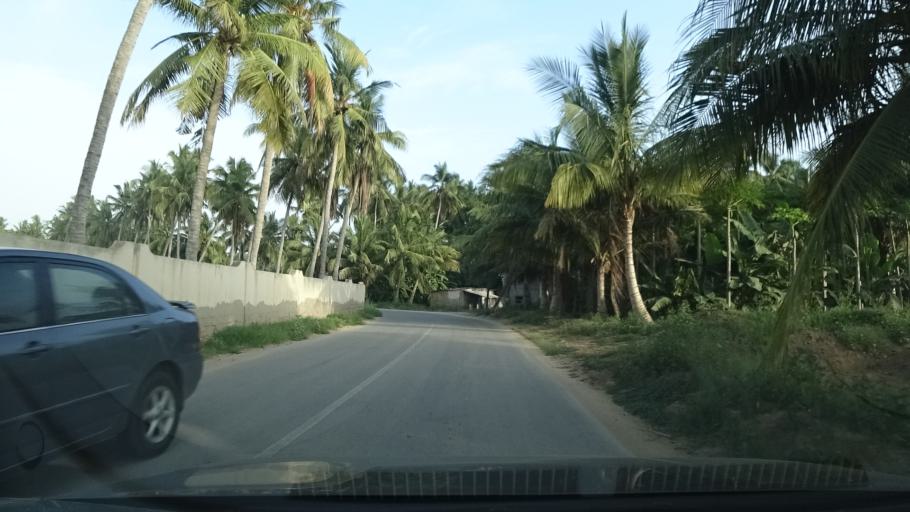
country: OM
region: Zufar
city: Salalah
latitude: 17.0175
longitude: 54.1397
